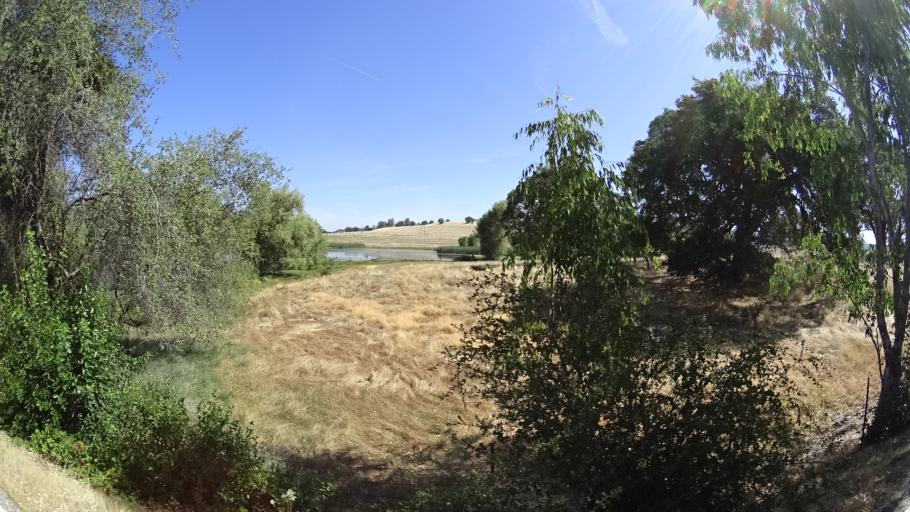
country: US
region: California
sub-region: Calaveras County
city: Valley Springs
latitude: 38.2285
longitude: -120.8383
